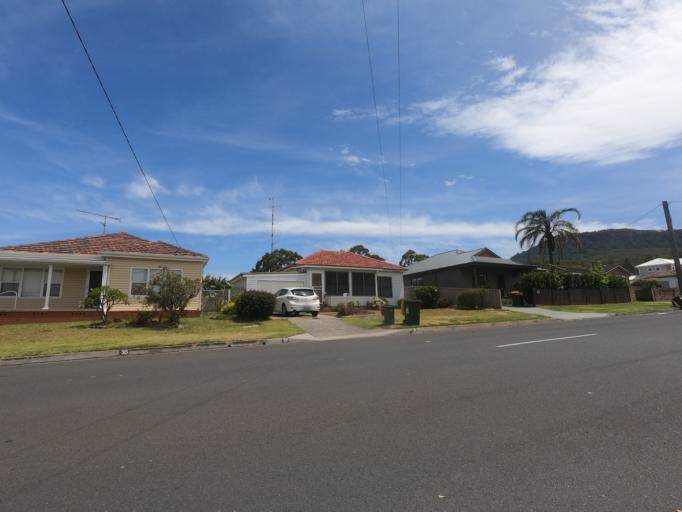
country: AU
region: New South Wales
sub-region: Wollongong
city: Mount Ousley
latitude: -34.3948
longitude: 150.8809
